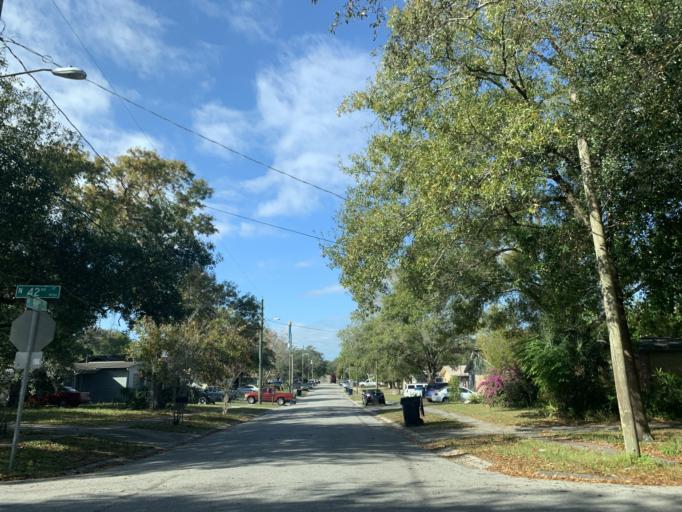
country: US
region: Florida
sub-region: Hillsborough County
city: Temple Terrace
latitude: 28.0384
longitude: -82.4120
